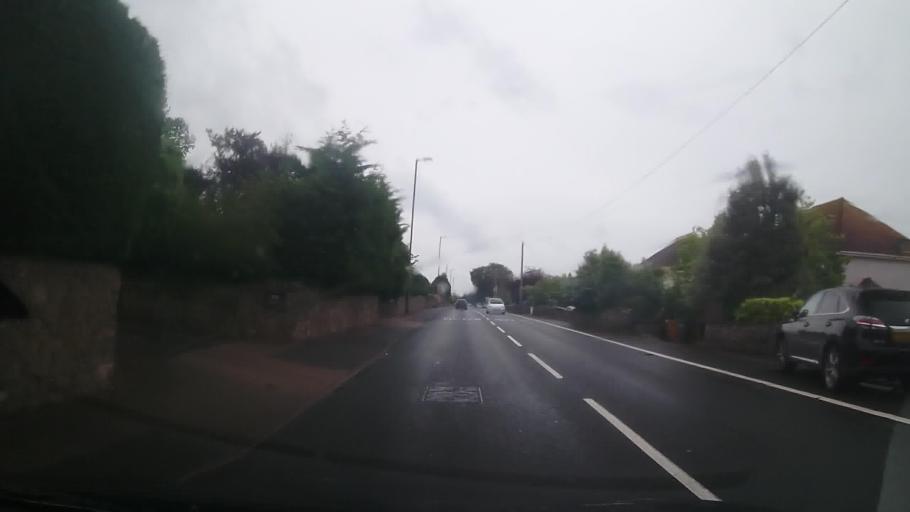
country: GB
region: England
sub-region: Borough of Torbay
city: Paignton
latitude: 50.4056
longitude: -3.5647
